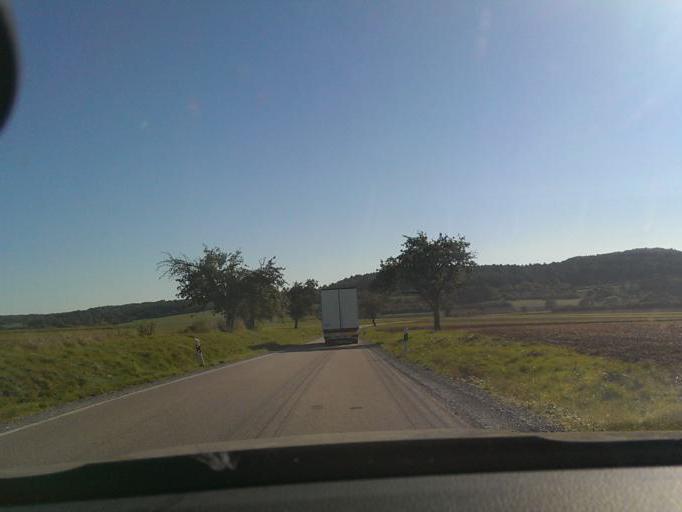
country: DE
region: Baden-Wuerttemberg
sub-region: Karlsruhe Region
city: Friolzheim
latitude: 48.8241
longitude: 8.8232
